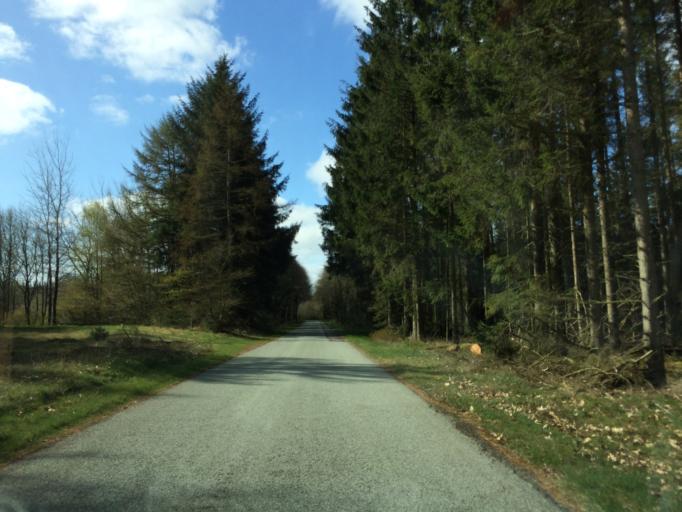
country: DK
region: Central Jutland
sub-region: Holstebro Kommune
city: Ulfborg
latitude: 56.2058
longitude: 8.4509
